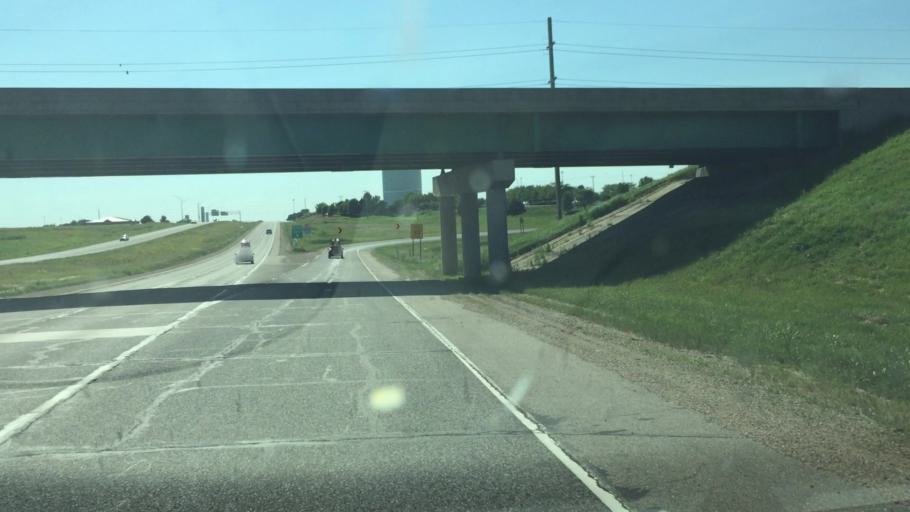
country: US
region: Iowa
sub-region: Linn County
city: Ely
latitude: 41.9268
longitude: -91.6370
